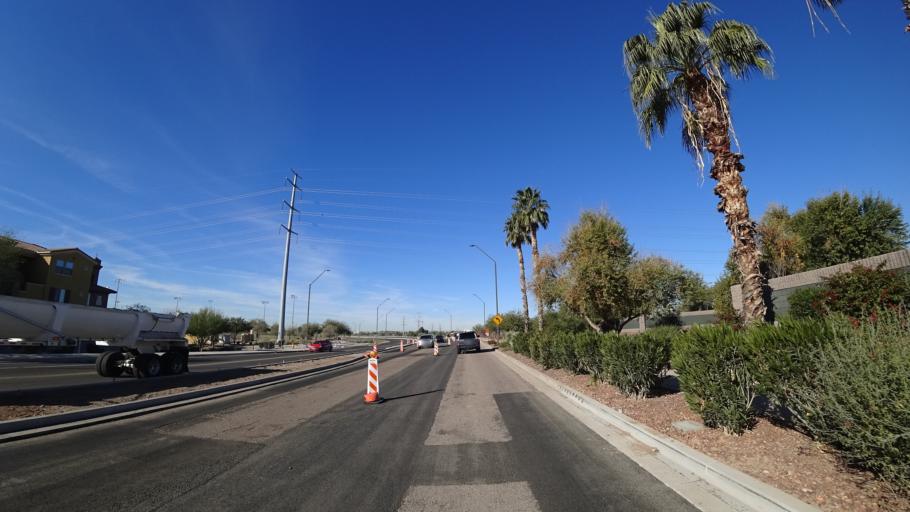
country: US
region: Arizona
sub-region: Maricopa County
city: Avondale
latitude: 33.4641
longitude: -112.3185
